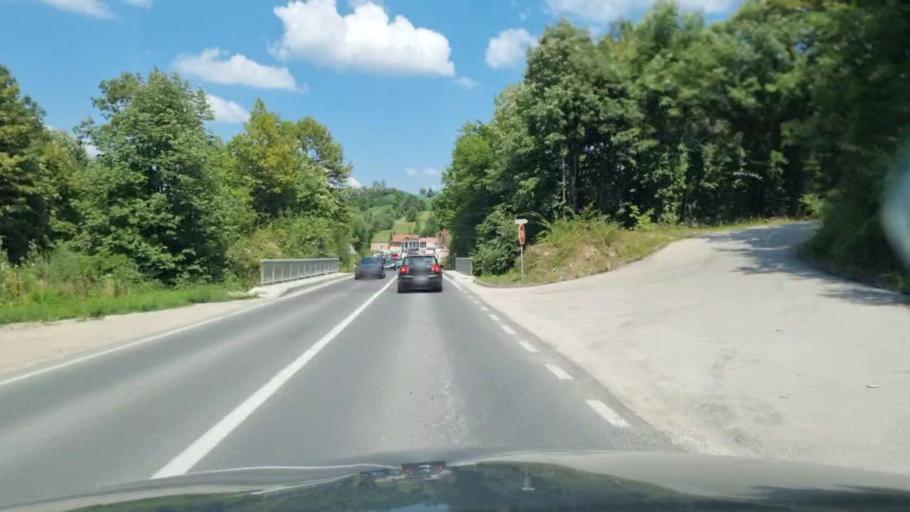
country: BA
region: Federation of Bosnia and Herzegovina
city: Srebrenik
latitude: 44.6872
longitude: 18.5035
